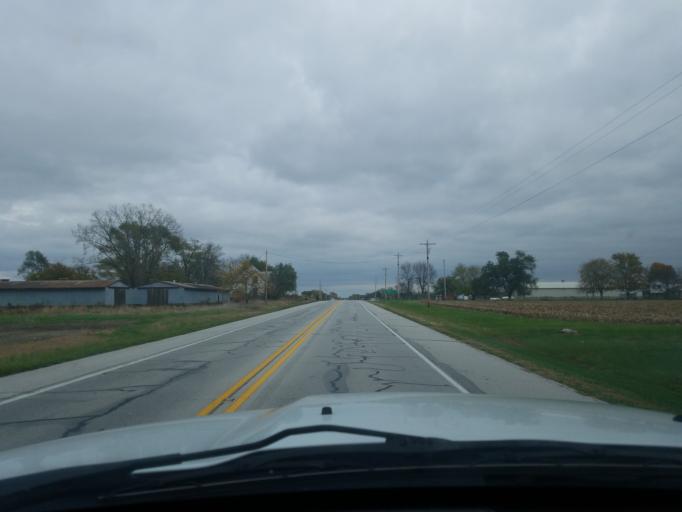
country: US
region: Indiana
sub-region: Shelby County
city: Shelbyville
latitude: 39.4958
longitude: -85.8985
